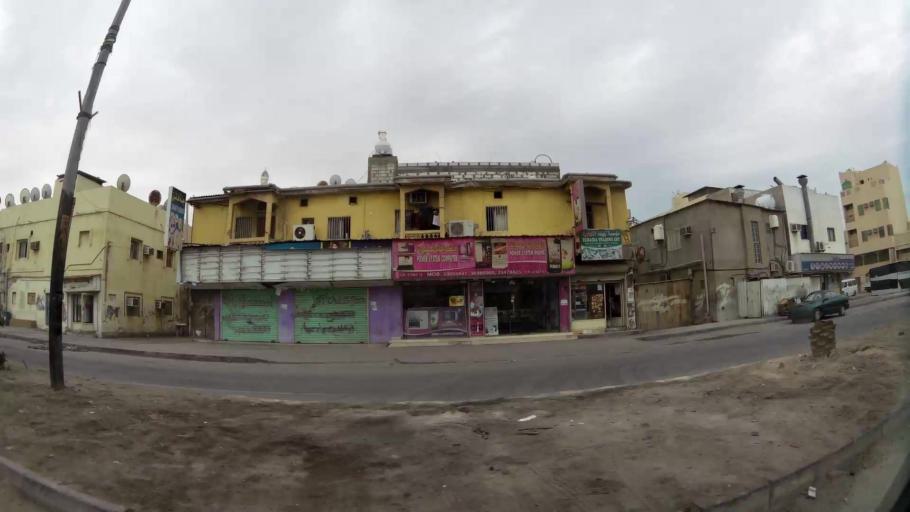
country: BH
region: Northern
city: Sitrah
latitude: 26.1632
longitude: 50.6161
